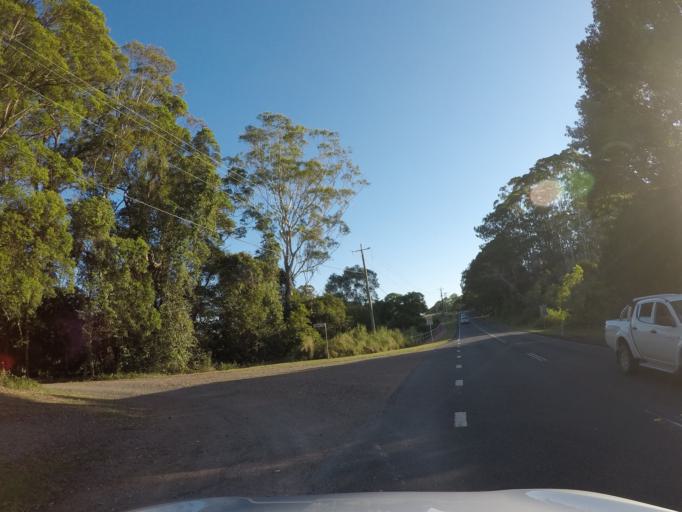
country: AU
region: Queensland
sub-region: Sunshine Coast
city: Nambour
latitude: -26.6330
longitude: 152.8578
